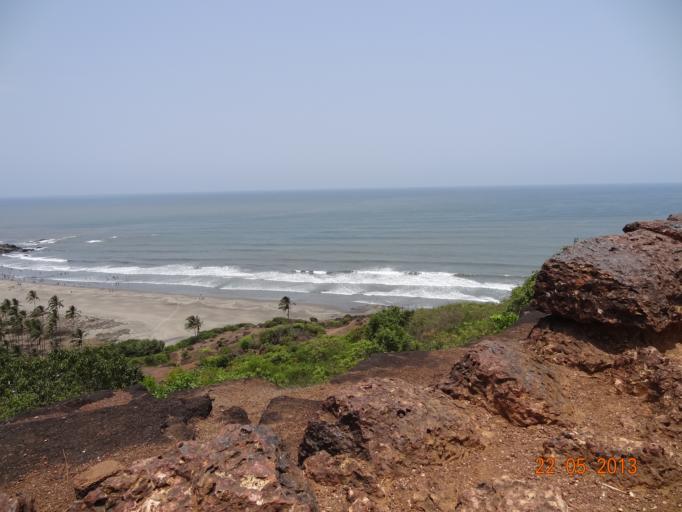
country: IN
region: Goa
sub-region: North Goa
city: Vagator
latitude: 15.6053
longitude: 73.7351
